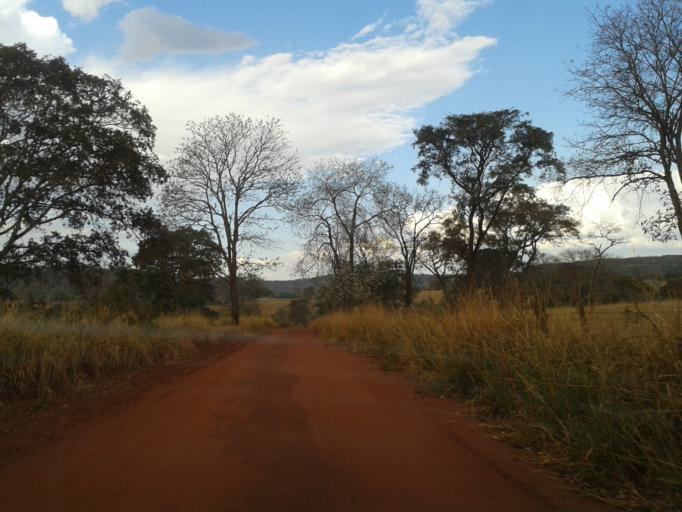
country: BR
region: Minas Gerais
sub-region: Santa Vitoria
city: Santa Vitoria
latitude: -19.2010
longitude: -49.9052
